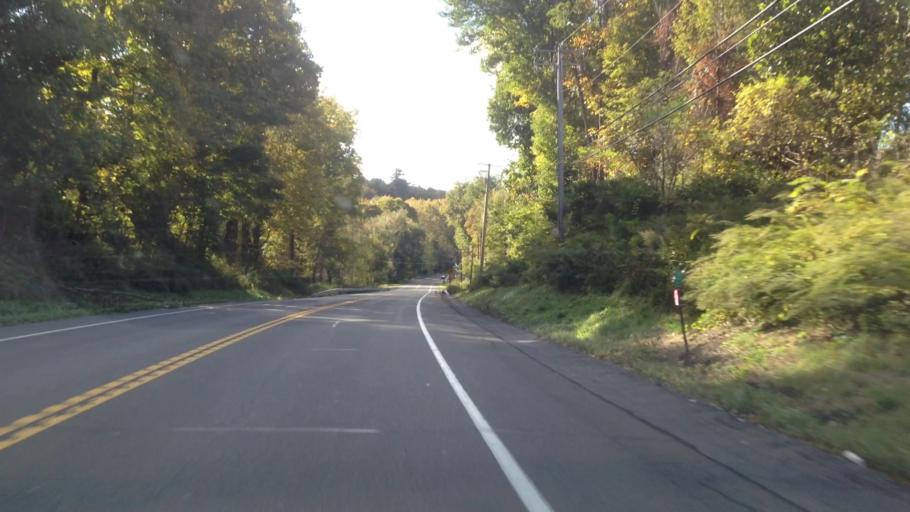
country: US
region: New York
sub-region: Dutchess County
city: Hyde Park
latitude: 41.8229
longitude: -73.9652
